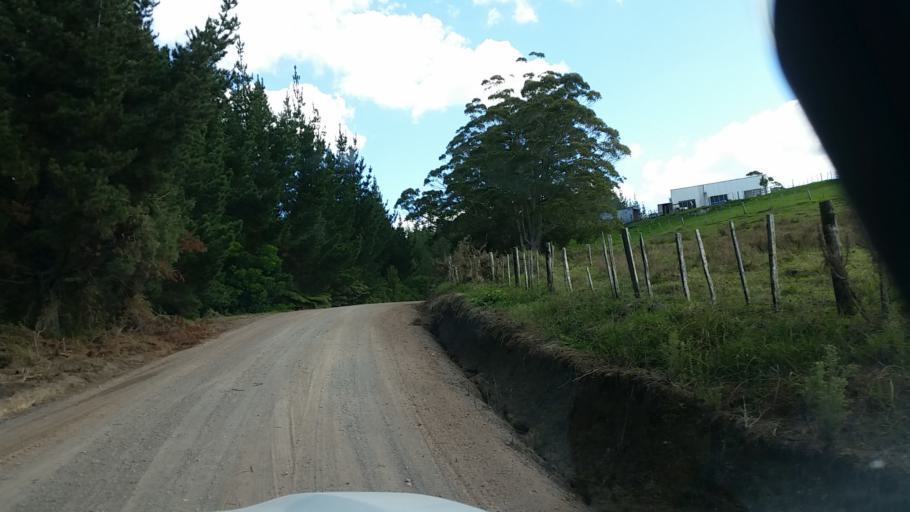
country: NZ
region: Northland
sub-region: Whangarei
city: Whangarei
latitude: -35.5956
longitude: 174.3215
